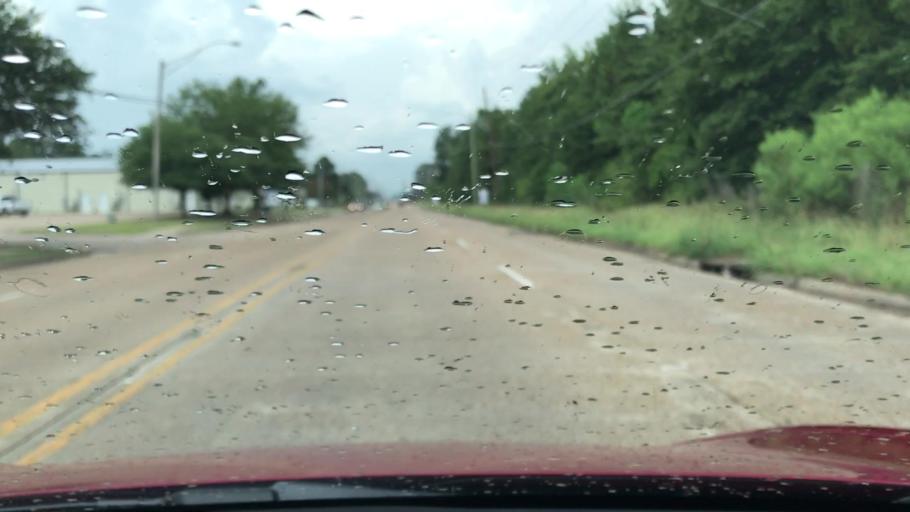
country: US
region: Louisiana
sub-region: Bossier Parish
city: Bossier City
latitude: 32.4092
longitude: -93.7632
